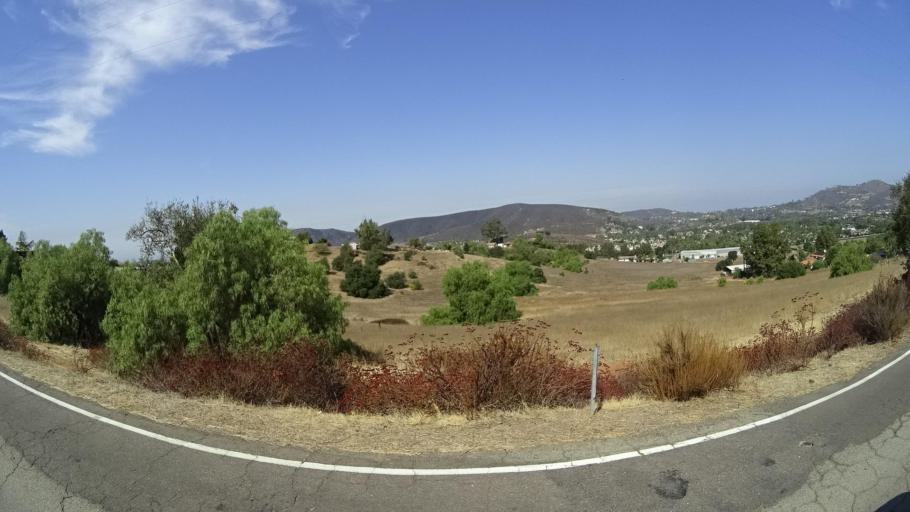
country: US
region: California
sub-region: San Diego County
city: San Marcos
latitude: 33.1658
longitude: -117.1458
